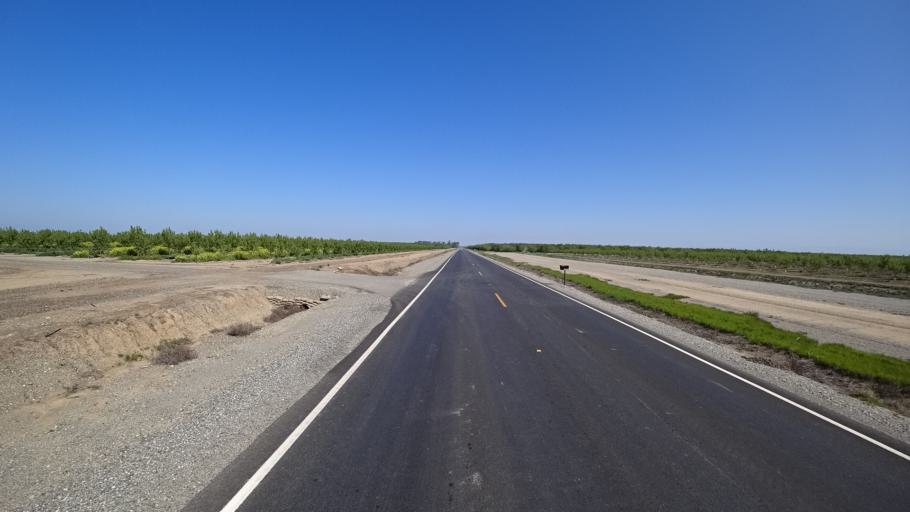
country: US
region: California
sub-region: Glenn County
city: Hamilton City
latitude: 39.6451
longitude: -122.0650
